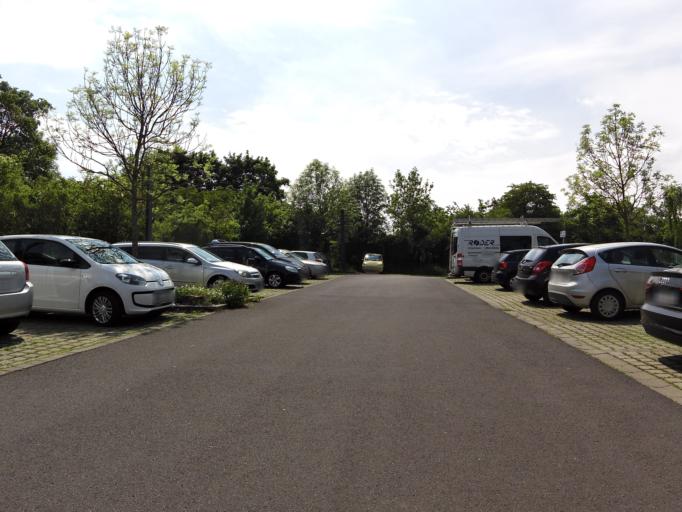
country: DE
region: Bavaria
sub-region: Regierungsbezirk Unterfranken
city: Wuerzburg
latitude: 49.7824
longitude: 9.9634
